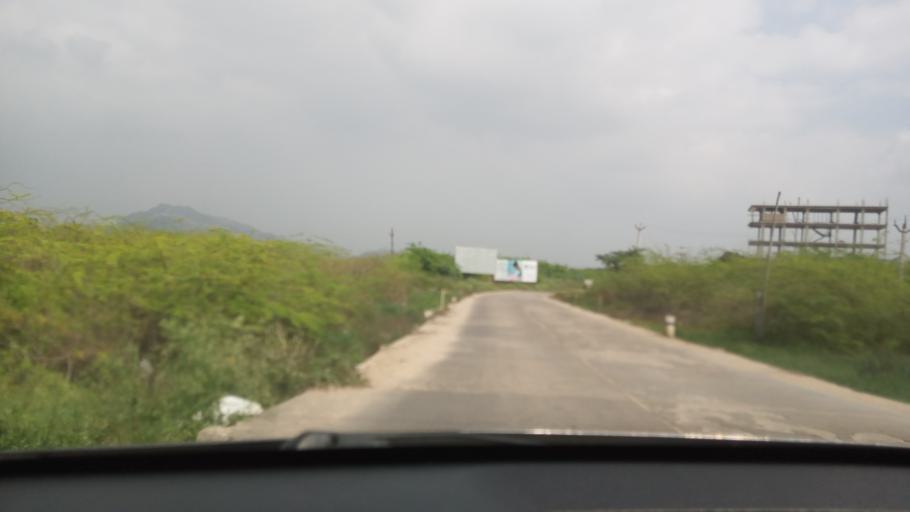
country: IN
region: Andhra Pradesh
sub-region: Chittoor
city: Madanapalle
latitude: 13.6520
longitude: 78.8102
